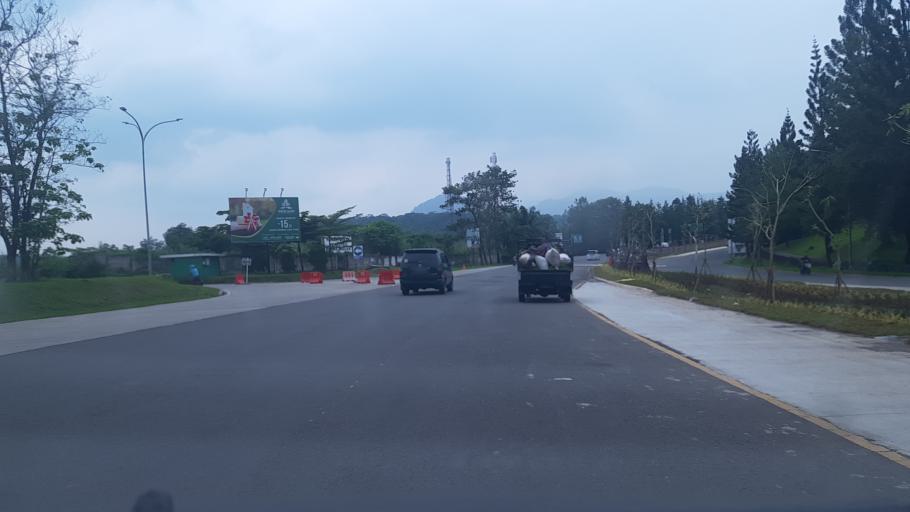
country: ID
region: West Java
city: Bogor
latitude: -6.5683
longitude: 106.8602
